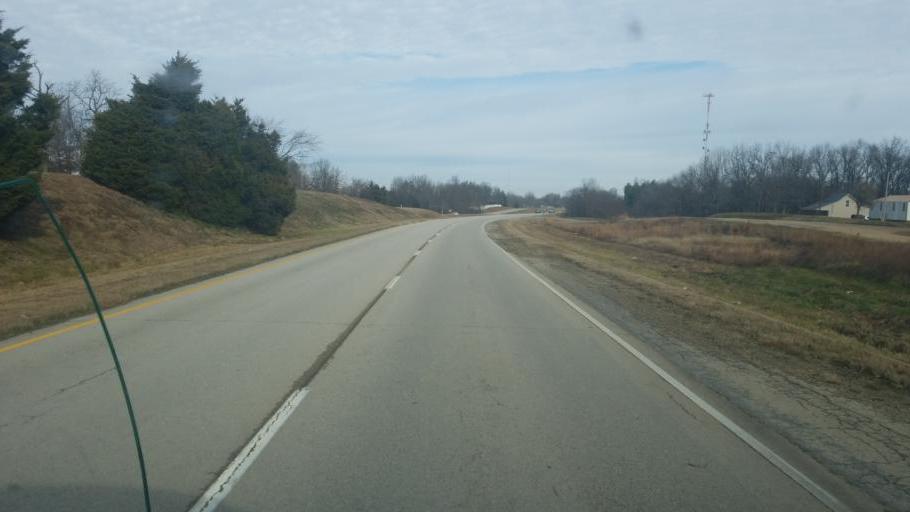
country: US
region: Missouri
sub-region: Stoddard County
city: Dexter
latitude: 36.8385
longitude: -89.9419
